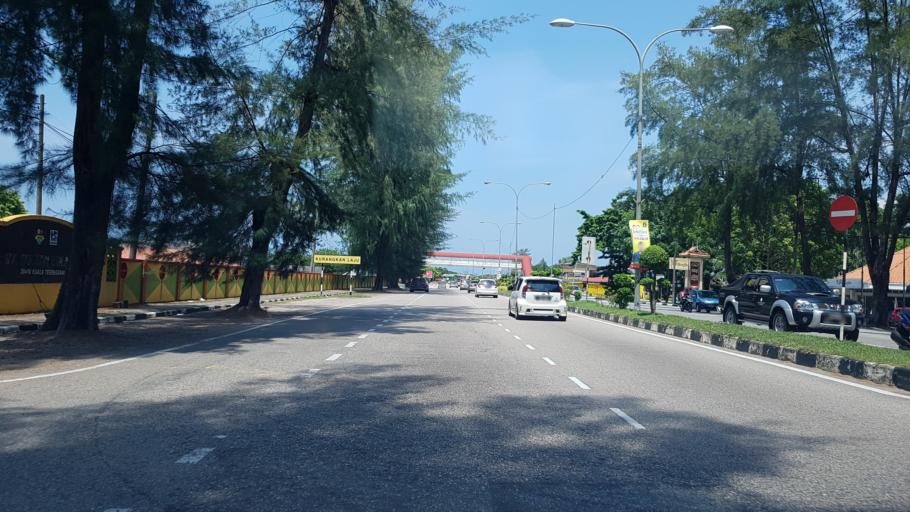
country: MY
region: Terengganu
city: Kuala Terengganu
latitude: 5.3009
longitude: 103.1628
